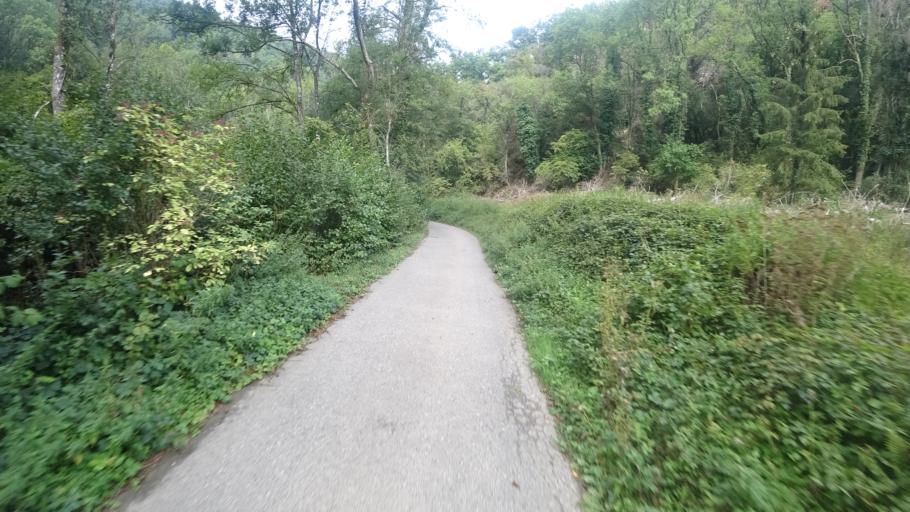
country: DE
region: Rheinland-Pfalz
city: Morshausen
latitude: 50.2094
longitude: 7.4528
